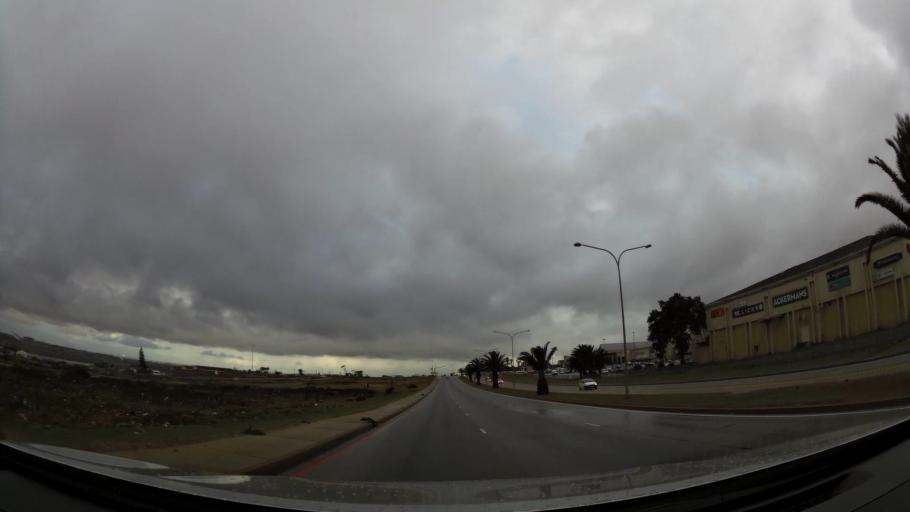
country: ZA
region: Eastern Cape
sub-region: Nelson Mandela Bay Metropolitan Municipality
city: Port Elizabeth
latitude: -33.8935
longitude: 25.5283
